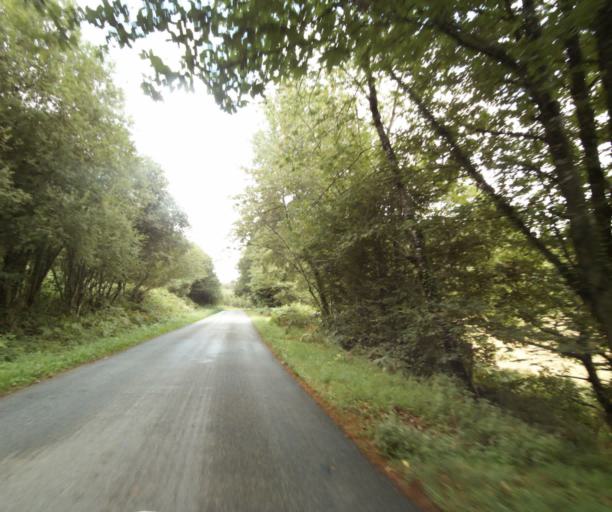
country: FR
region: Limousin
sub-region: Departement de la Correze
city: Sainte-Fortunade
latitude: 45.1967
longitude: 1.7857
